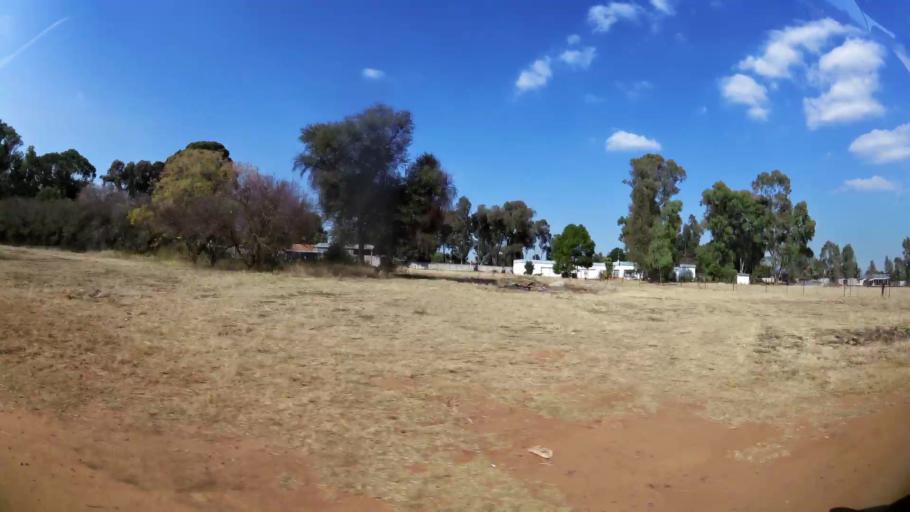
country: ZA
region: Gauteng
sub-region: Ekurhuleni Metropolitan Municipality
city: Benoni
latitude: -26.0803
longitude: 28.3478
